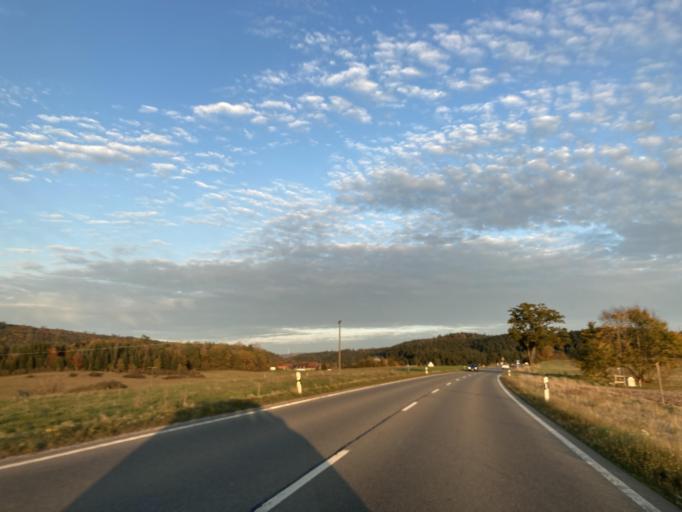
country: DE
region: Baden-Wuerttemberg
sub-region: Freiburg Region
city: Dietingen
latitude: 48.1818
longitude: 8.6505
